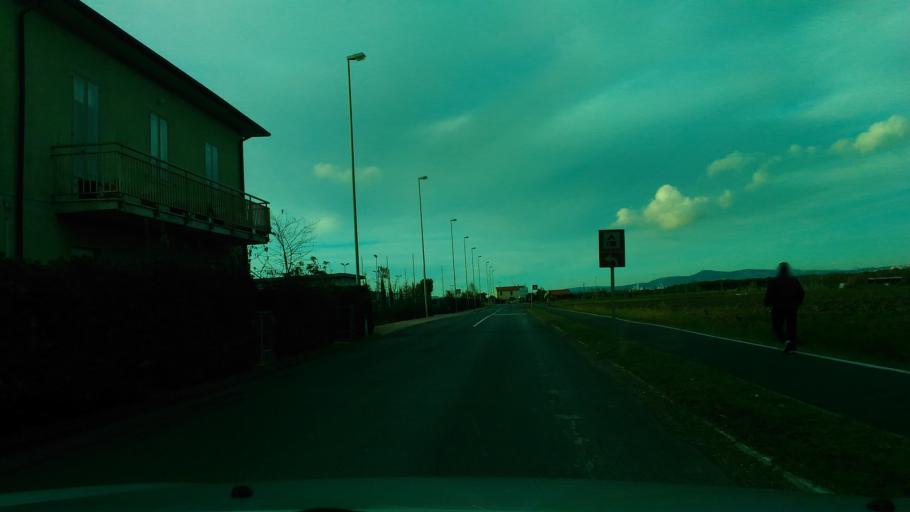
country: IT
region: Tuscany
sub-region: Provincia di Livorno
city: S.P. in Palazzi
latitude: 43.3087
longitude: 10.4891
